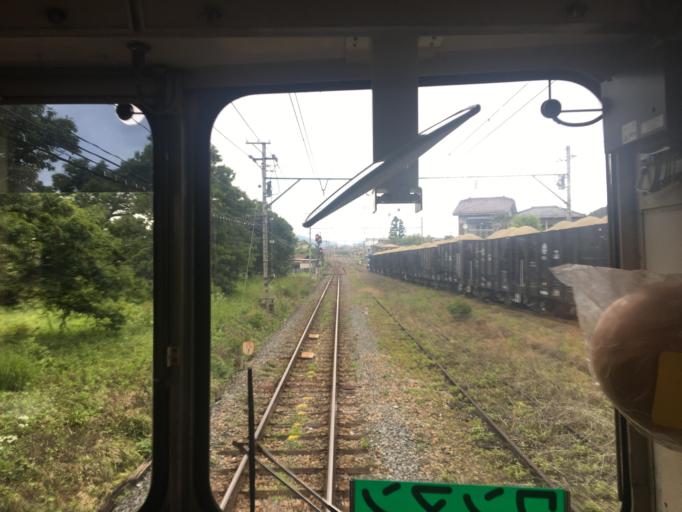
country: JP
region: Saitama
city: Chichibu
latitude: 35.9687
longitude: 139.0659
